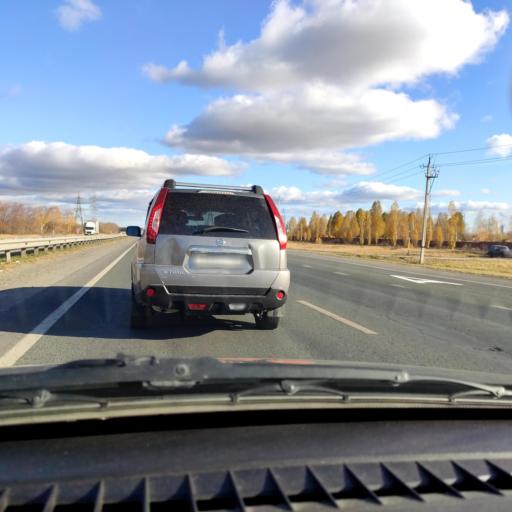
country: RU
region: Samara
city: Tol'yatti
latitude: 53.5769
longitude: 49.4267
